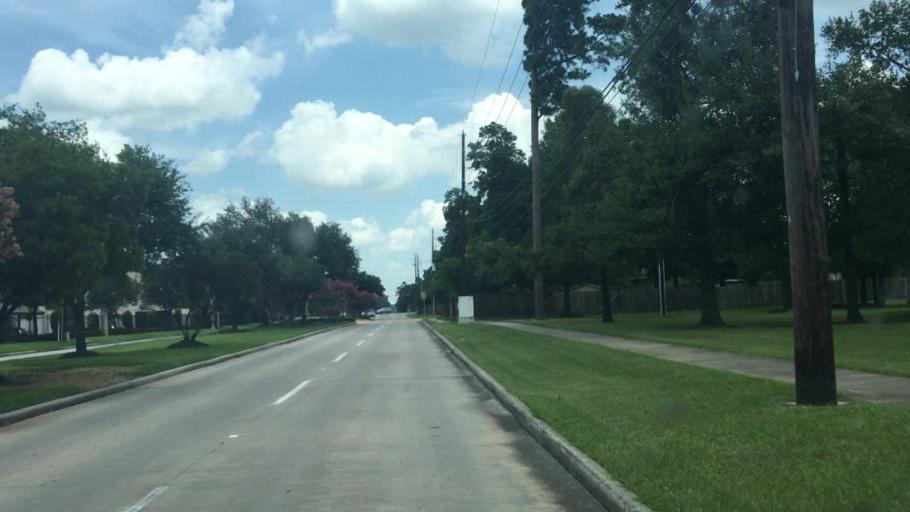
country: US
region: Texas
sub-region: Harris County
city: Atascocita
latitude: 29.9796
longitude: -95.2122
